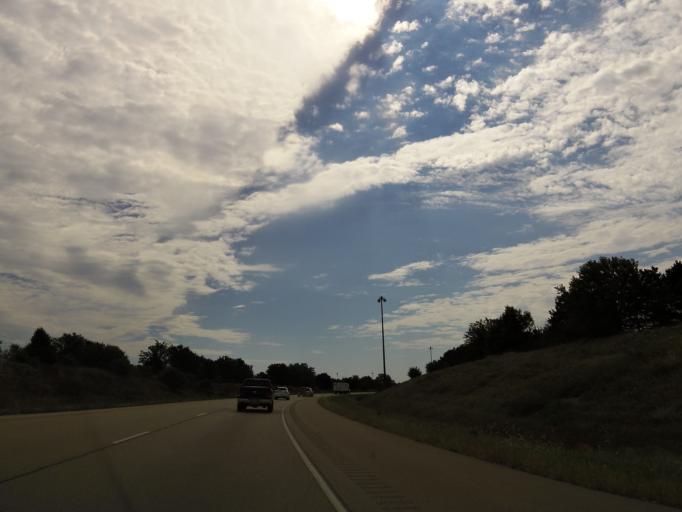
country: US
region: Illinois
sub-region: McLean County
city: Normal
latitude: 40.5387
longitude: -89.0147
